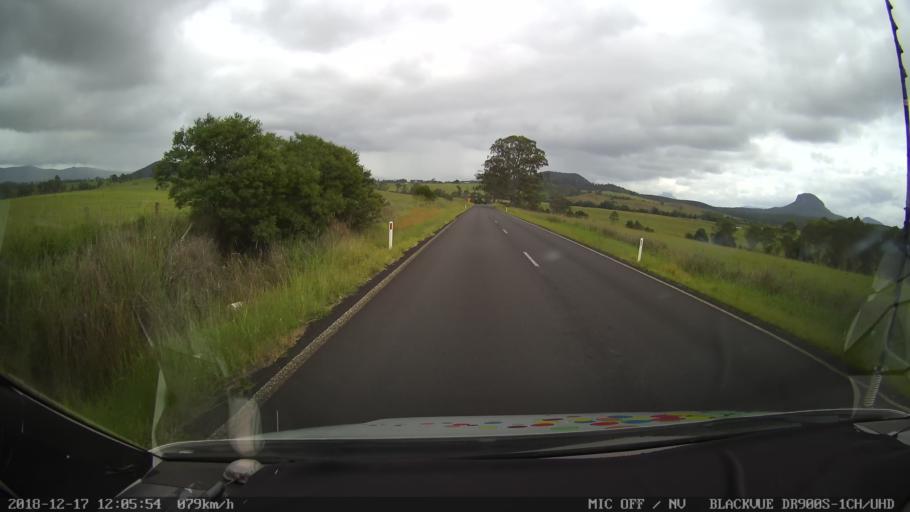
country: AU
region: New South Wales
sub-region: Kyogle
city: Kyogle
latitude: -28.4877
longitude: 152.5671
